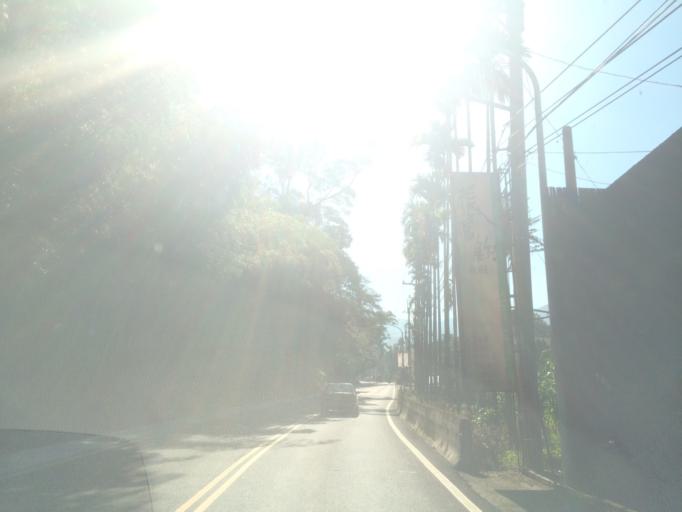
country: TW
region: Taiwan
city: Lugu
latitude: 23.7275
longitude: 120.7754
